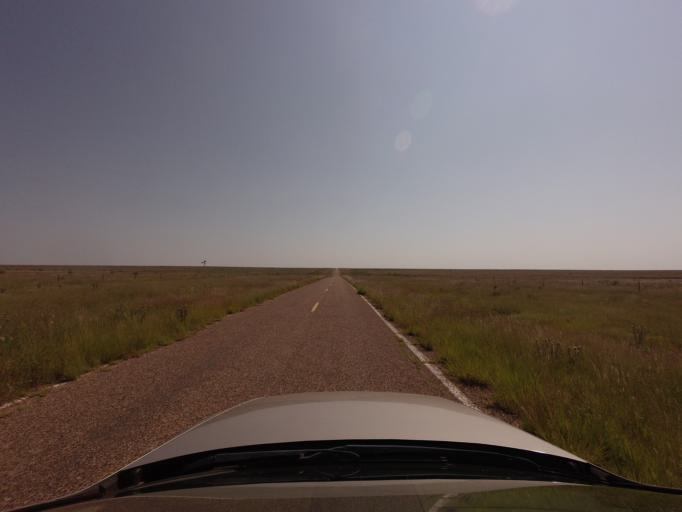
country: US
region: New Mexico
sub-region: Curry County
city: Cannon Air Force Base
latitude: 34.6330
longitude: -103.4036
